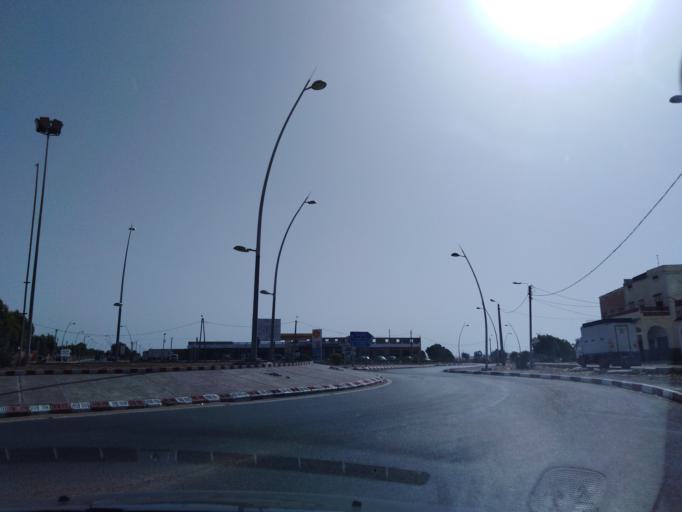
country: MA
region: Doukkala-Abda
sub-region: Safi
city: Safi
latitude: 32.2540
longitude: -8.9824
